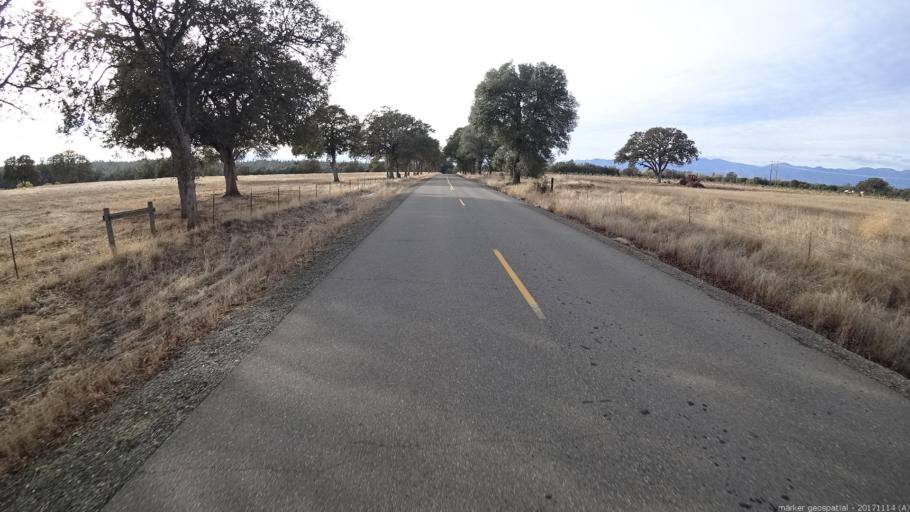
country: US
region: California
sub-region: Shasta County
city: Anderson
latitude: 40.3880
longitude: -122.4865
